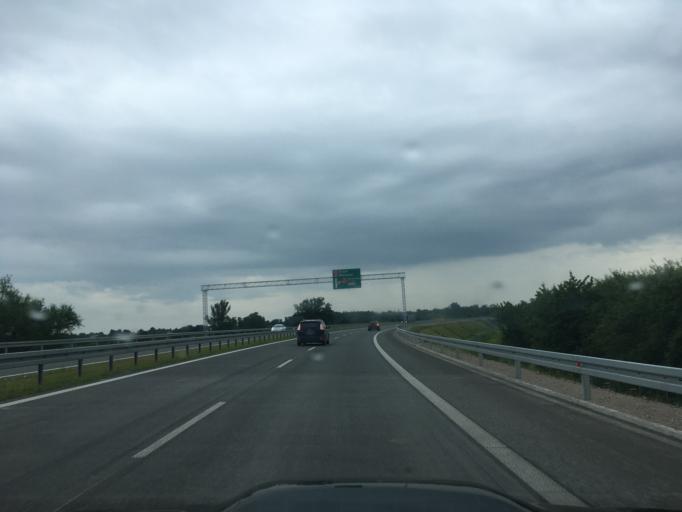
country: PL
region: Masovian Voivodeship
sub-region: Powiat piaseczynski
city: Gora Kalwaria
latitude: 51.9757
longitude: 21.2244
